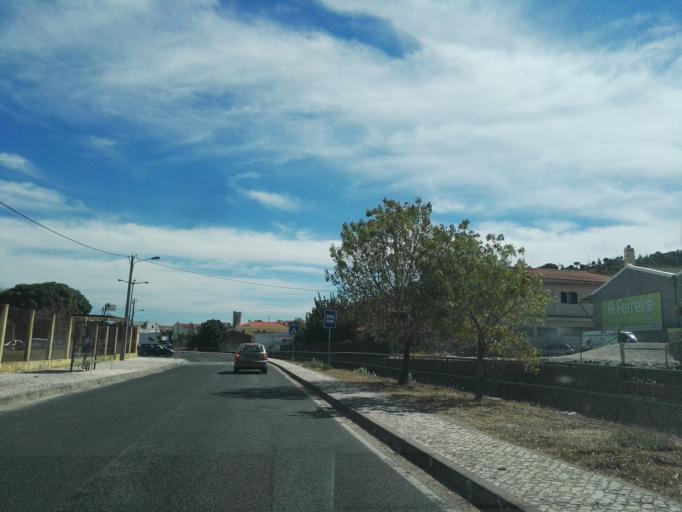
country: PT
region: Lisbon
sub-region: Vila Franca de Xira
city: Sao Joao dos Montes
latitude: 38.9320
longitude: -9.0187
